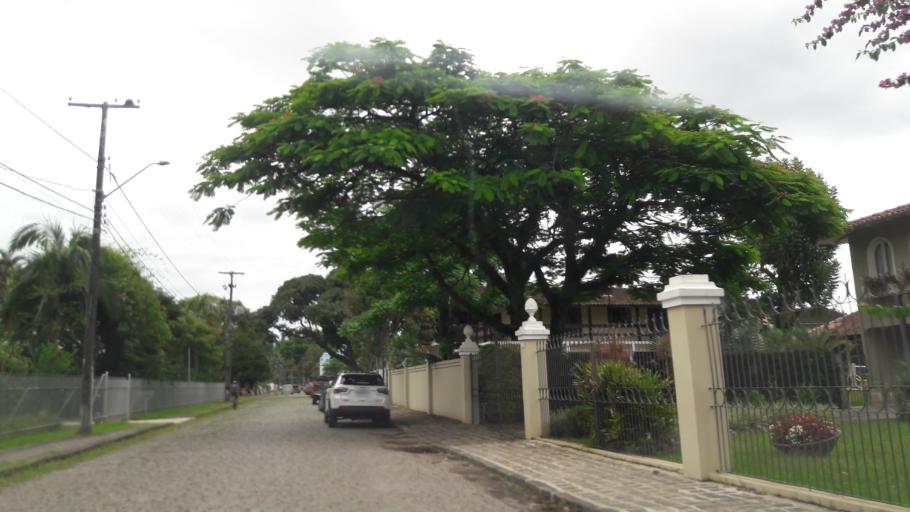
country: BR
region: Parana
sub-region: Antonina
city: Antonina
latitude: -25.4762
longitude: -48.8305
